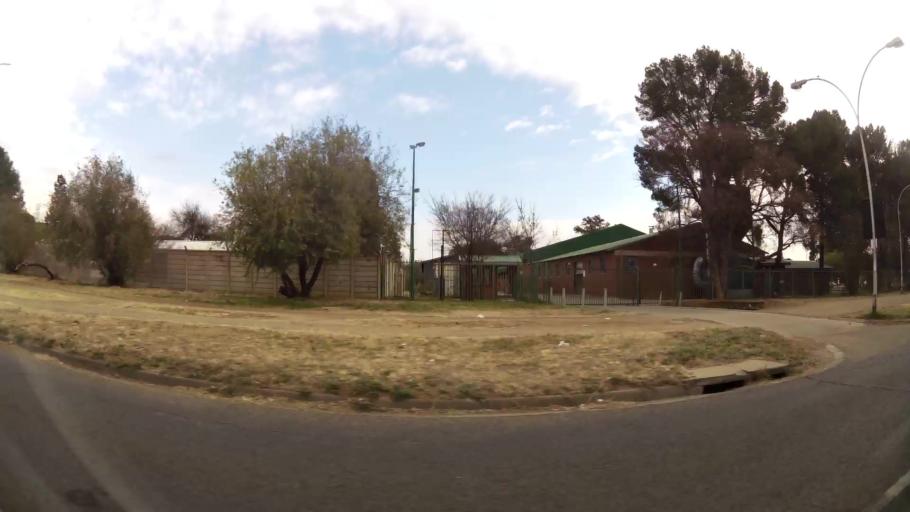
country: ZA
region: Orange Free State
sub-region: Mangaung Metropolitan Municipality
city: Bloemfontein
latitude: -29.1061
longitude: 26.1878
